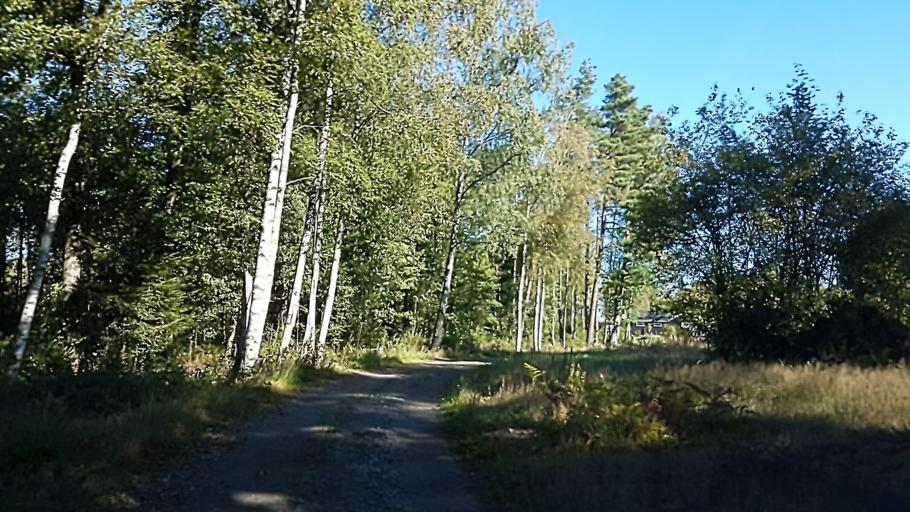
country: SE
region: Kronoberg
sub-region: Ljungby Kommun
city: Ljungby
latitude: 56.8099
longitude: 14.0030
